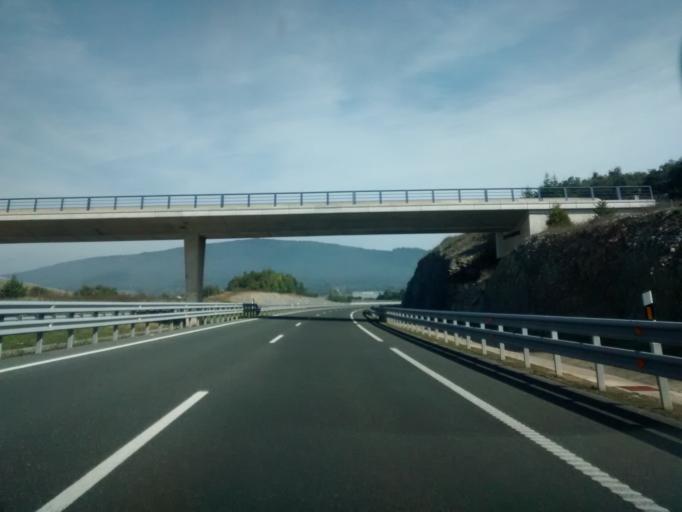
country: ES
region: Basque Country
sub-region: Provincia de Guipuzcoa
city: Leintz-Gatzaga
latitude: 42.9510
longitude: -2.6271
